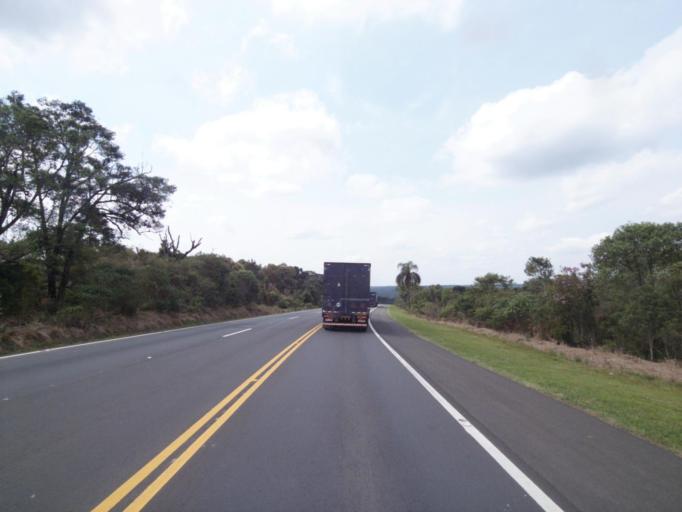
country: BR
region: Parana
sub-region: Irati
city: Irati
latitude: -25.4642
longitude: -50.4628
